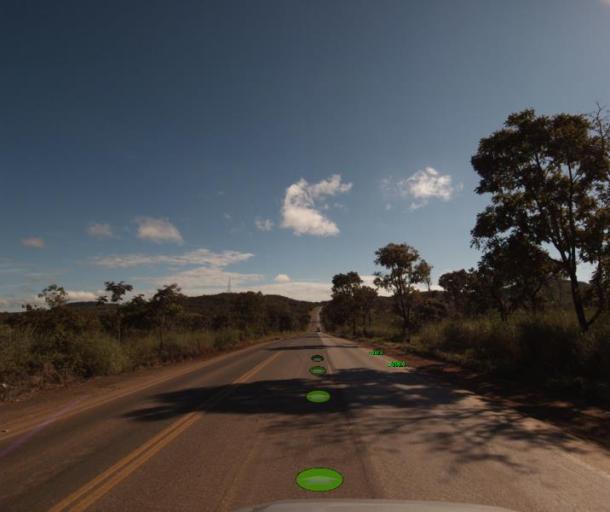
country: BR
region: Goias
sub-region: Uruacu
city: Uruacu
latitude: -14.5833
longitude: -49.1603
